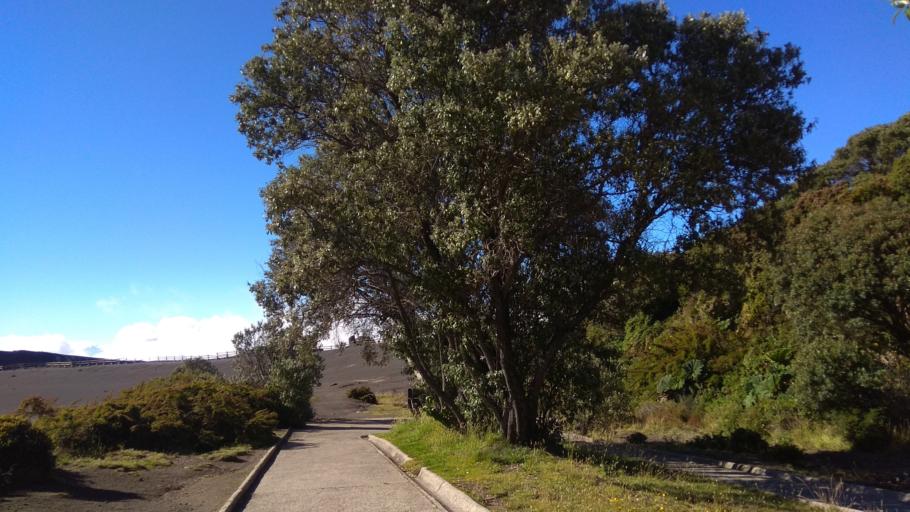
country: CR
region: Cartago
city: Cot
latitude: 9.9786
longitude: -83.8465
